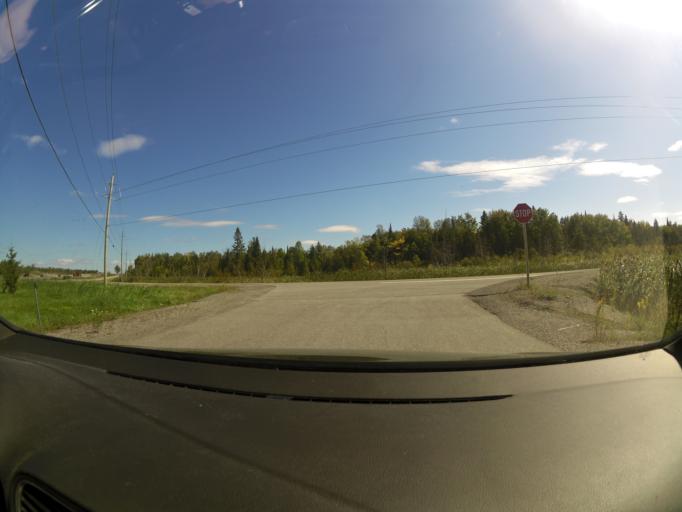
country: CA
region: Ontario
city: Carleton Place
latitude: 45.2060
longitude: -76.0342
